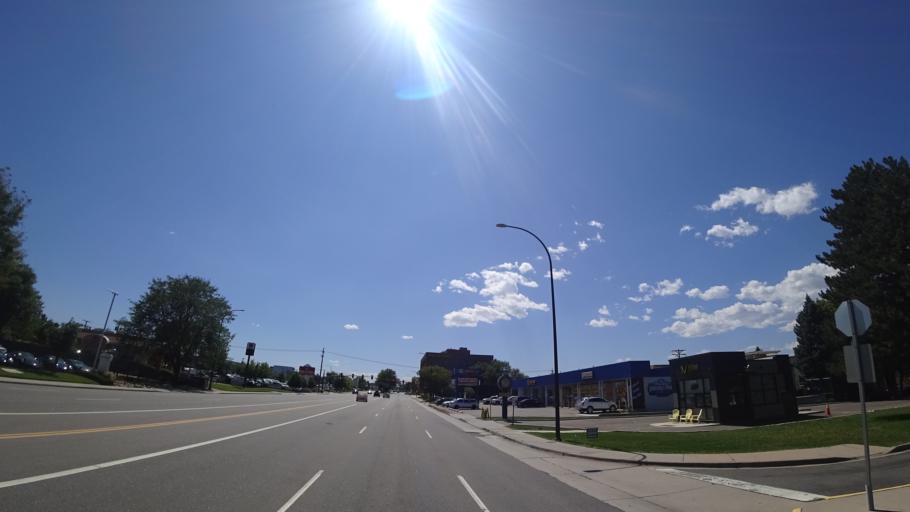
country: US
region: Colorado
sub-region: Arapahoe County
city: Littleton
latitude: 39.6164
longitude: -104.9881
